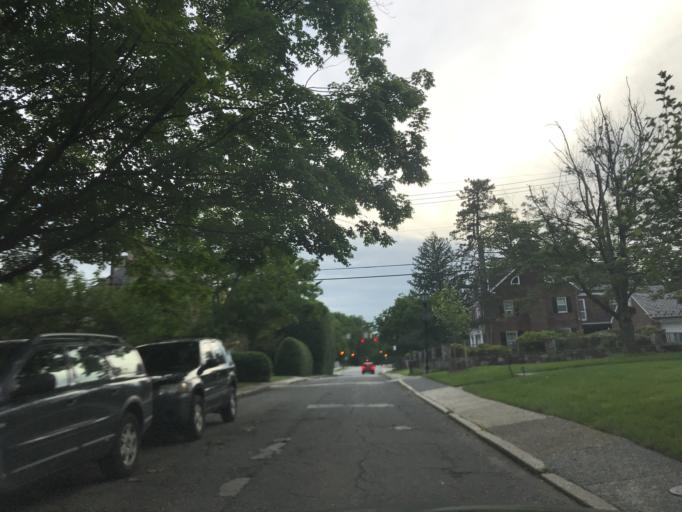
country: US
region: Maryland
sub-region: Baltimore County
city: Towson
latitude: 39.3596
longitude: -76.6230
